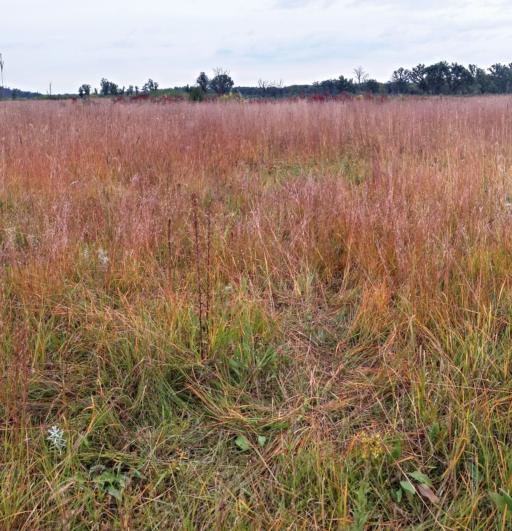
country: US
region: Wisconsin
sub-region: Pepin County
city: Durand
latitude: 44.7331
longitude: -91.8486
